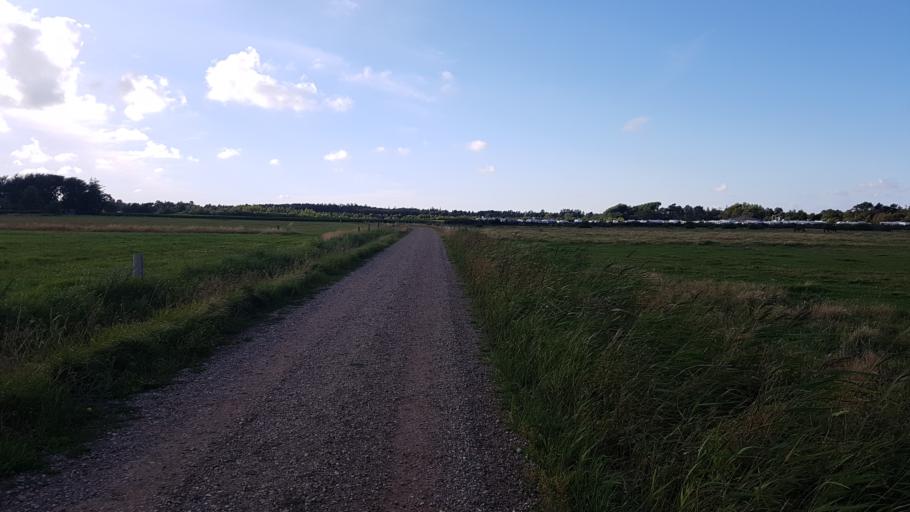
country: DE
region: Schleswig-Holstein
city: List
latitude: 55.0878
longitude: 8.5400
